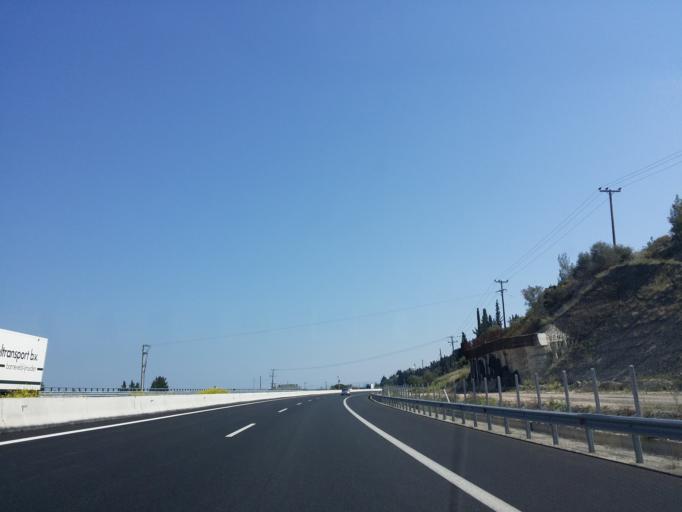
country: GR
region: Peloponnese
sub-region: Nomos Korinthias
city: Kato Dhiminio
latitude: 38.0398
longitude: 22.7078
